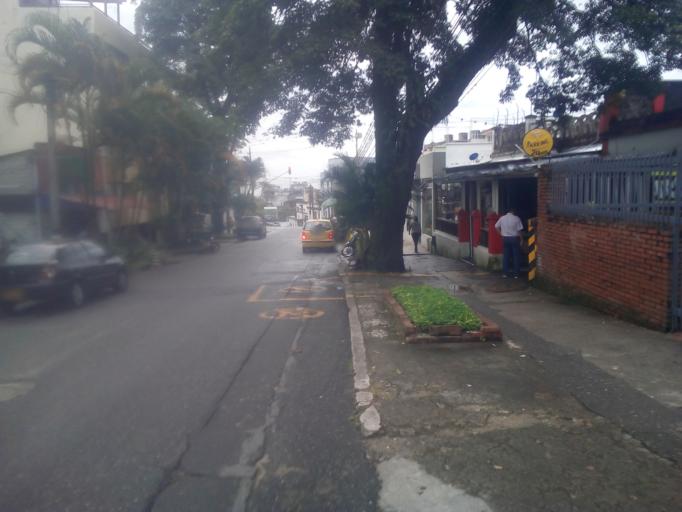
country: CO
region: Tolima
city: Ibague
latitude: 4.4479
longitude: -75.2416
